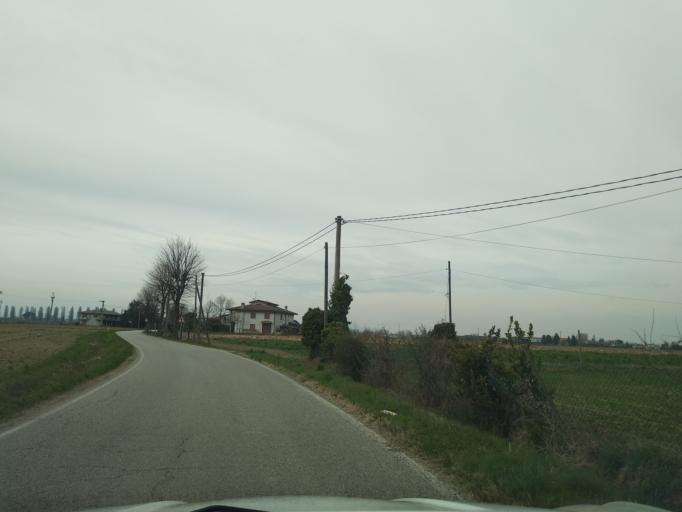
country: IT
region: Veneto
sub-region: Provincia di Padova
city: Saccolongo
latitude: 45.4092
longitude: 11.7621
